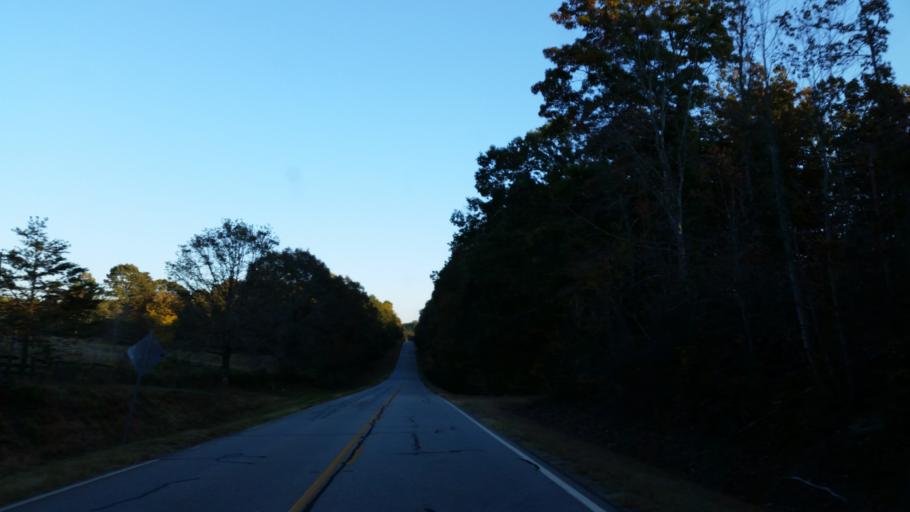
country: US
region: Georgia
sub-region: Lumpkin County
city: Dahlonega
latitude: 34.5272
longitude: -84.0554
